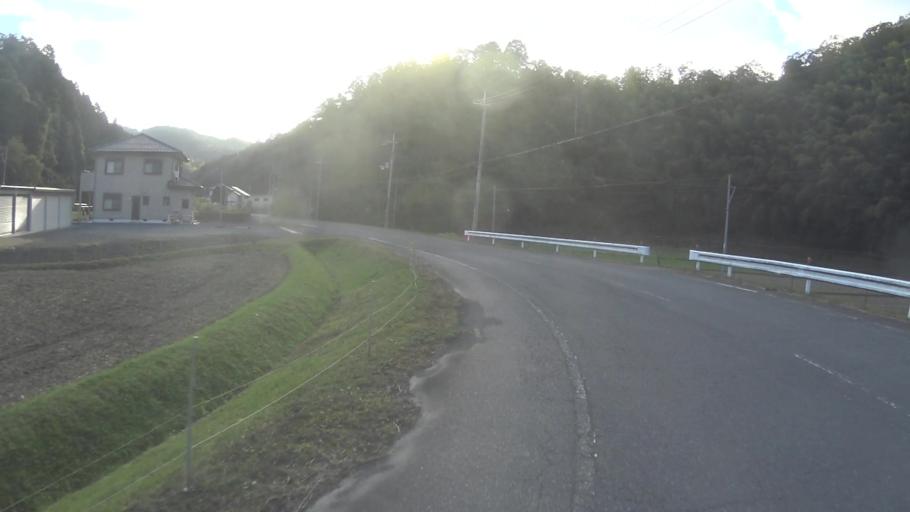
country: JP
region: Kyoto
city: Miyazu
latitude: 35.4606
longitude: 135.2327
